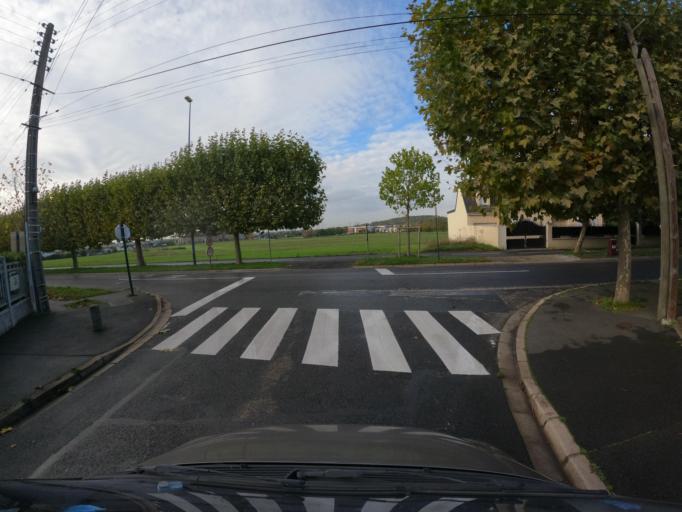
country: FR
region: Ile-de-France
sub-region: Departement de Seine-et-Marne
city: Brou-sur-Chantereine
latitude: 48.8913
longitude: 2.6187
